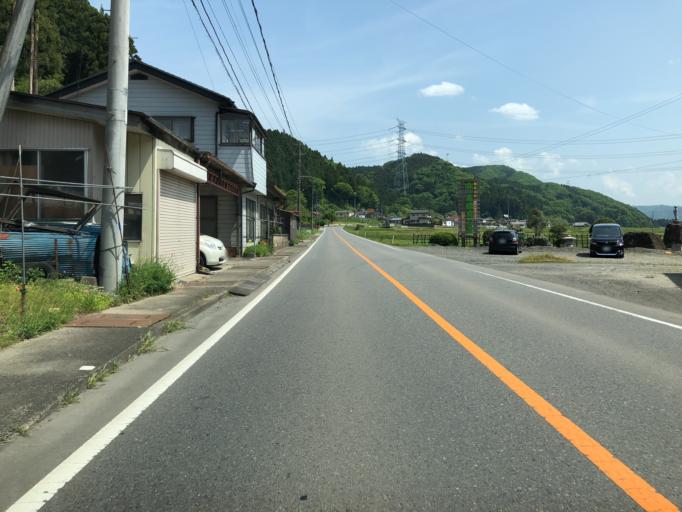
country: JP
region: Fukushima
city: Ishikawa
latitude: 37.1236
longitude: 140.5000
